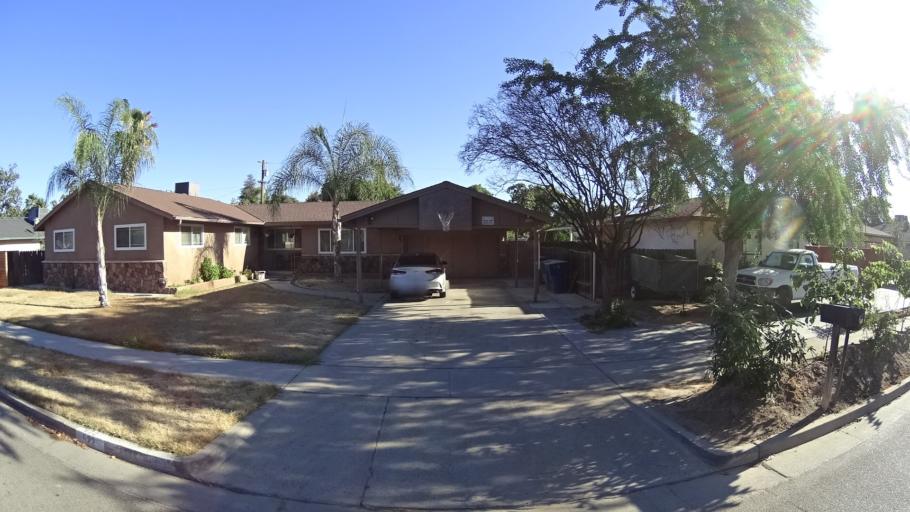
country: US
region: California
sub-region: Fresno County
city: Fresno
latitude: 36.8011
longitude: -119.8190
